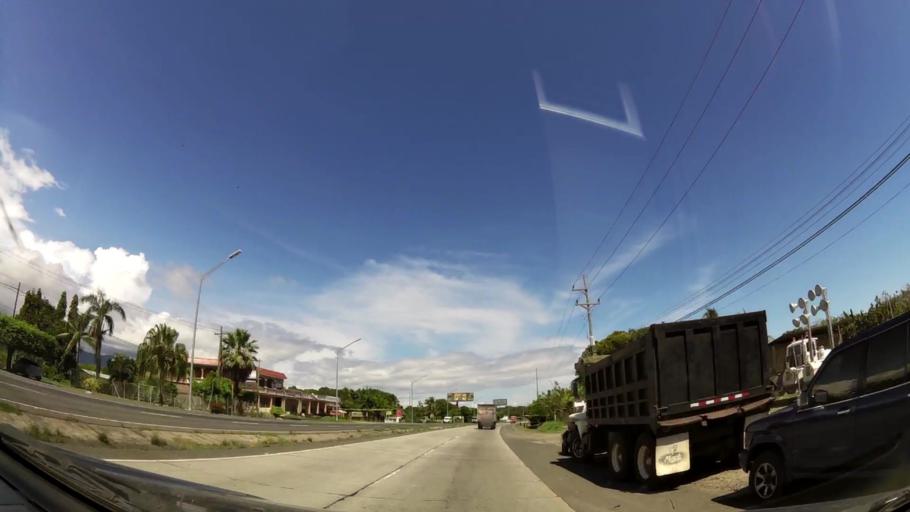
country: PA
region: Panama
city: Chame
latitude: 8.5578
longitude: -79.9041
